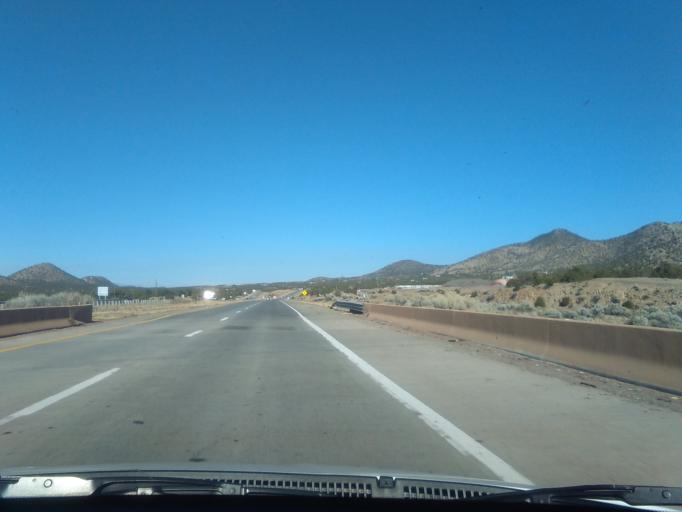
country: US
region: New Mexico
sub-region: Santa Fe County
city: Eldorado at Santa Fe
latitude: 35.5550
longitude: -105.8787
